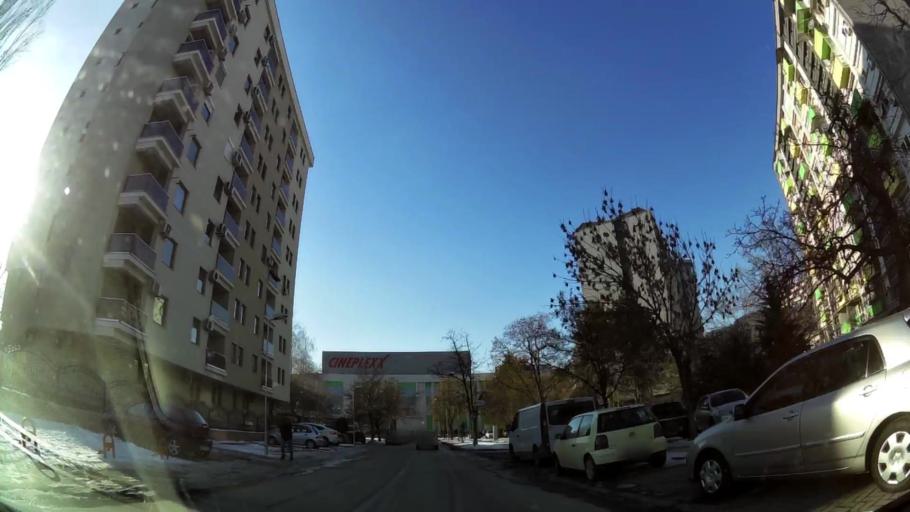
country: MK
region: Karpos
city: Skopje
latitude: 42.0047
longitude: 21.3944
